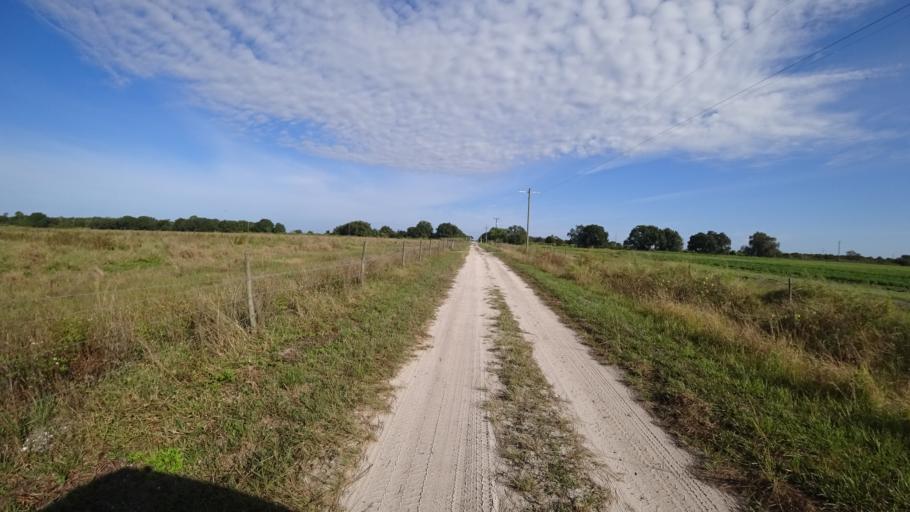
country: US
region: Florida
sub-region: Hillsborough County
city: Wimauma
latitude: 27.5978
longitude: -82.2928
